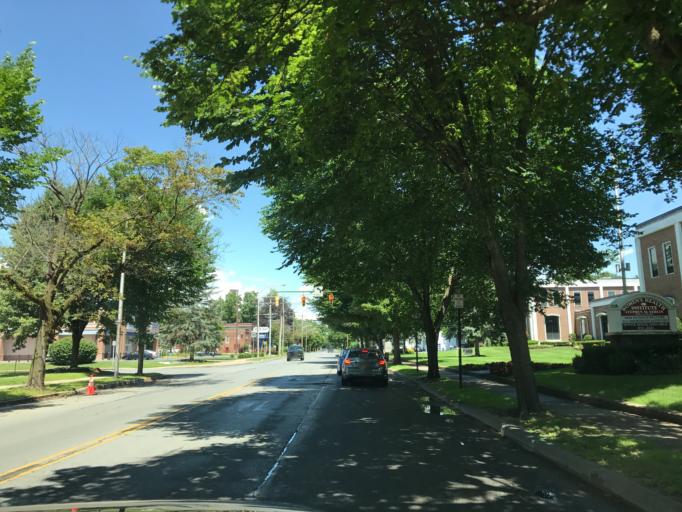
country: US
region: New York
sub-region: Warren County
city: Glens Falls
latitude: 43.3124
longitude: -73.6436
